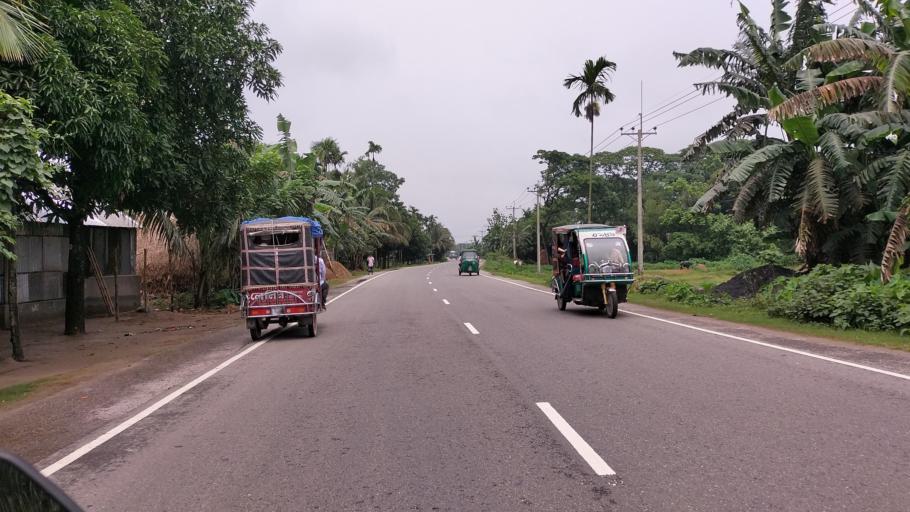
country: BD
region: Dhaka
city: Netrakona
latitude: 24.8501
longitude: 90.6383
